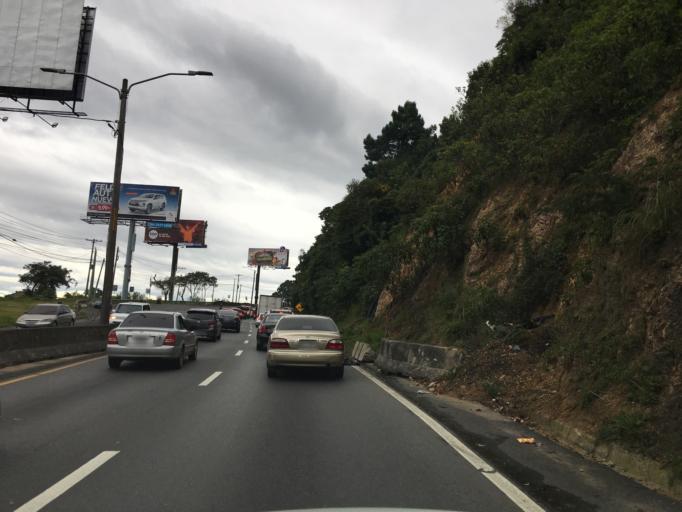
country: GT
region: Guatemala
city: Santa Catarina Pinula
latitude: 14.5783
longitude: -90.4775
